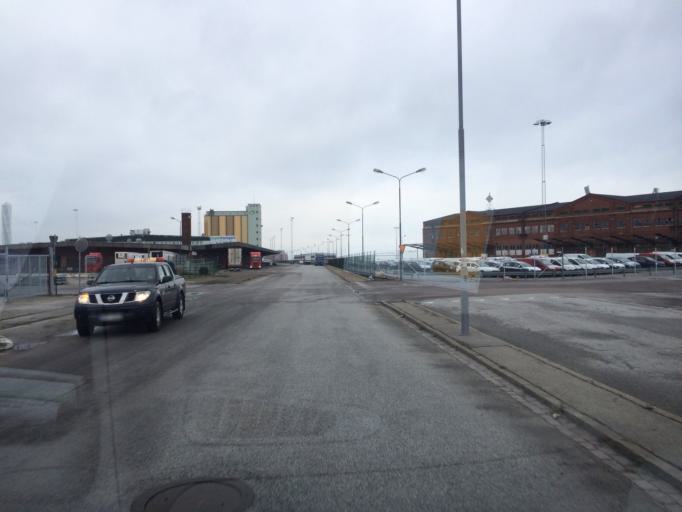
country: SE
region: Skane
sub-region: Malmo
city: Malmoe
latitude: 55.6142
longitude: 13.0084
